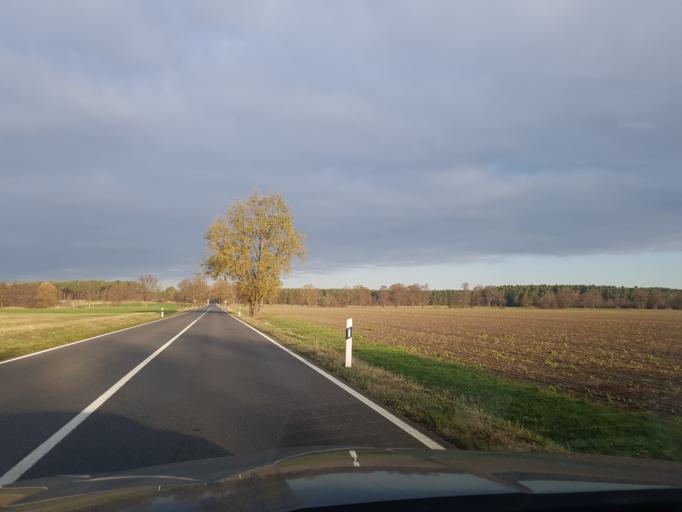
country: DE
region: Brandenburg
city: Kasel-Golzig
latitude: 51.9046
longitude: 13.6742
